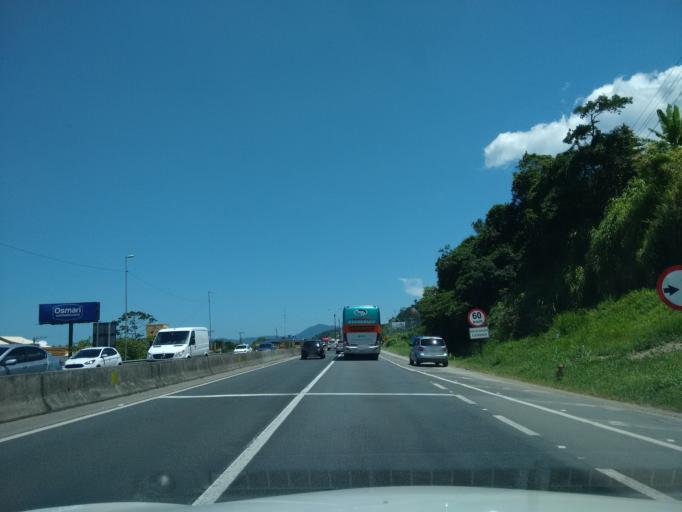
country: BR
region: Santa Catarina
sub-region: Itapema
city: Itapema
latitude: -27.0638
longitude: -48.5960
